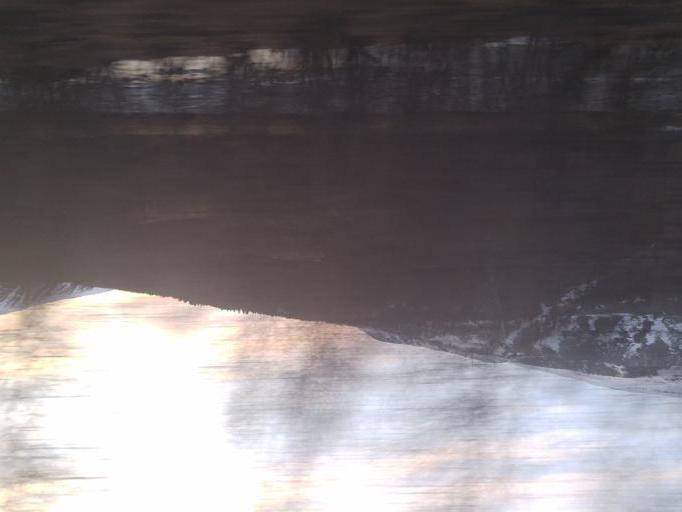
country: NO
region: Sor-Trondelag
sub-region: Oppdal
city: Oppdal
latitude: 62.4668
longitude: 9.5752
